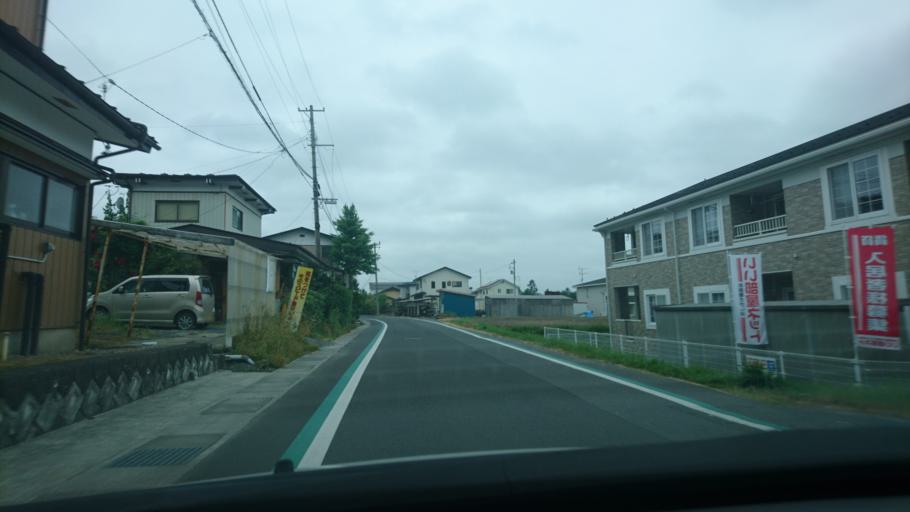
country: JP
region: Iwate
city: Ichinoseki
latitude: 38.9135
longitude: 141.1023
